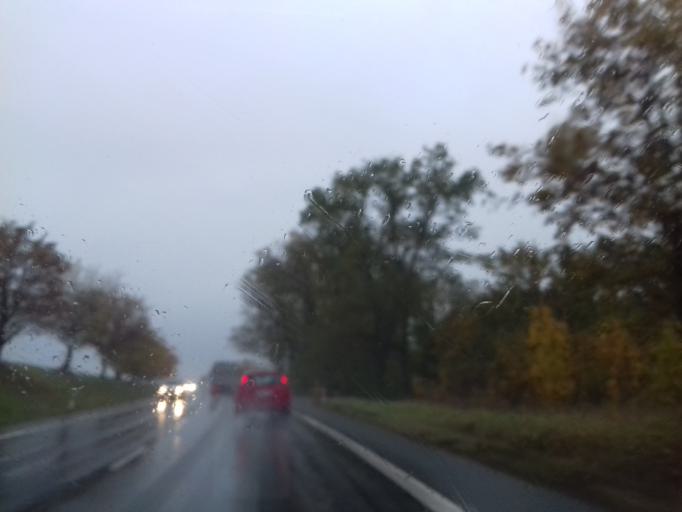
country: CZ
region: Pardubicky
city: Opatov
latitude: 49.7762
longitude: 16.5201
